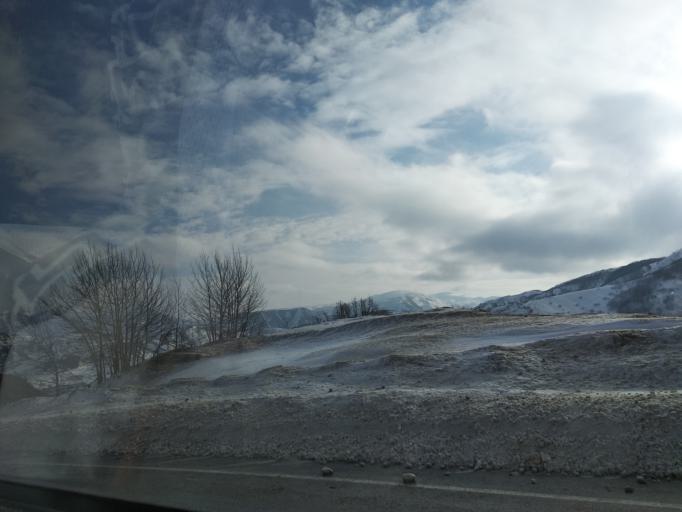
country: TR
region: Erzincan
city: Catalarmut
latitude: 39.8962
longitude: 39.3891
